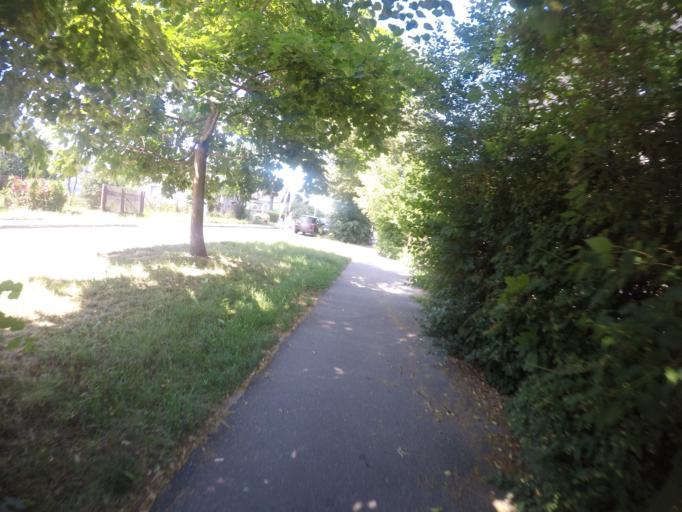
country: BY
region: Grodnenskaya
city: Hrodna
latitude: 53.6913
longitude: 23.8305
